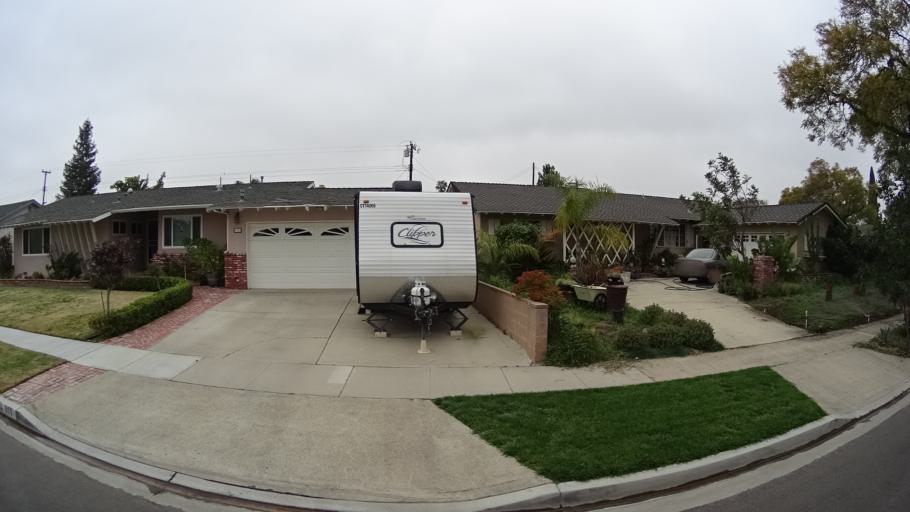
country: US
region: California
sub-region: Orange County
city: Stanton
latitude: 33.8210
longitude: -118.0048
